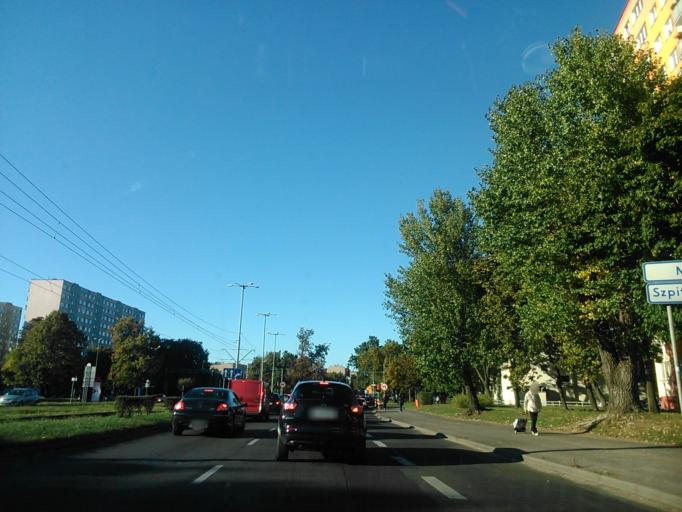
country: PL
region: Kujawsko-Pomorskie
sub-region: Torun
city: Torun
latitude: 53.0199
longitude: 18.6133
